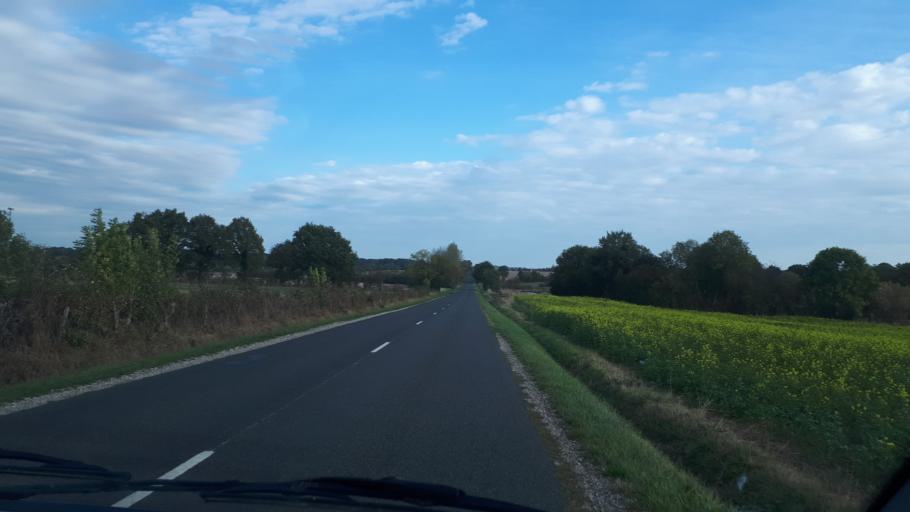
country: FR
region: Centre
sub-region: Departement du Loir-et-Cher
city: Mondoubleau
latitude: 47.9168
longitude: 0.9317
